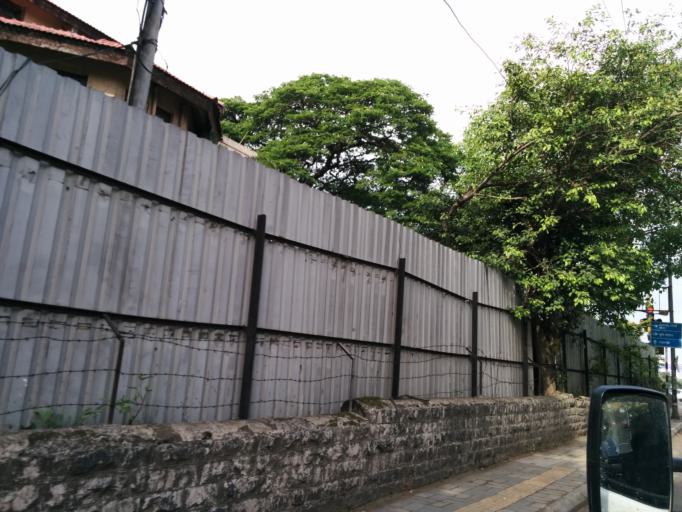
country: IN
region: Maharashtra
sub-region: Pune Division
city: Pune
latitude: 18.5029
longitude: 73.8792
